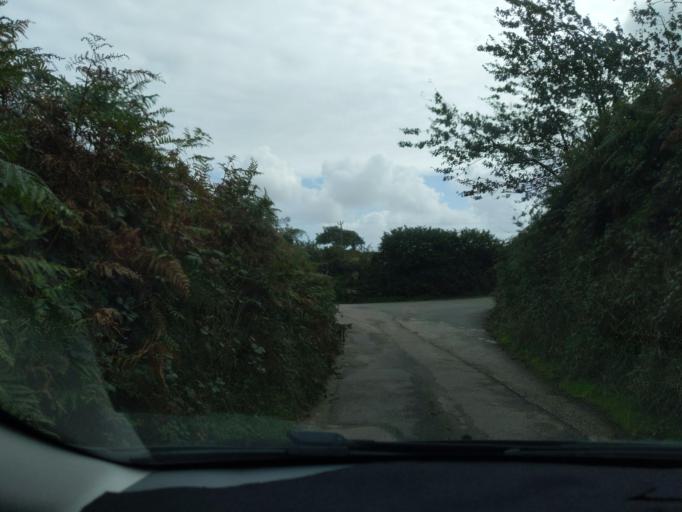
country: GB
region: England
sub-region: Cornwall
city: Par
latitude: 50.3905
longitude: -4.7039
